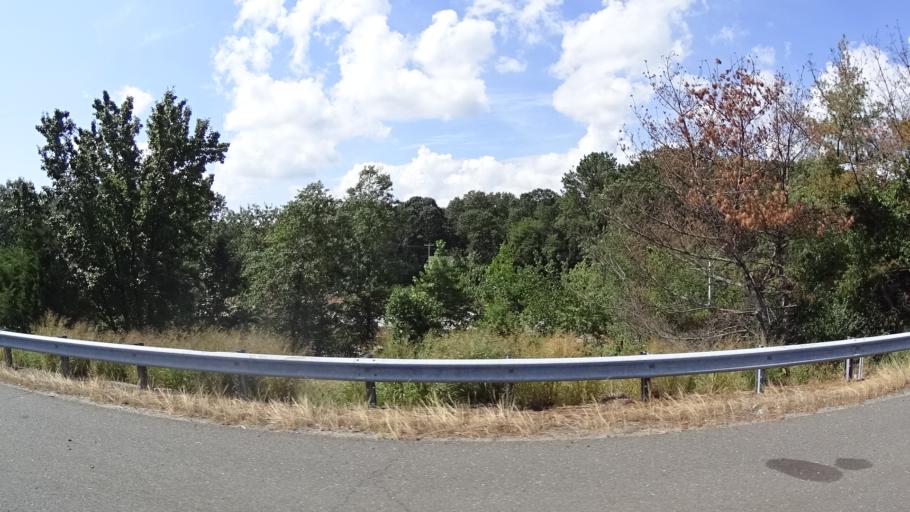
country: US
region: New Jersey
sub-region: Monmouth County
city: Eatontown
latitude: 40.2758
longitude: -74.0707
